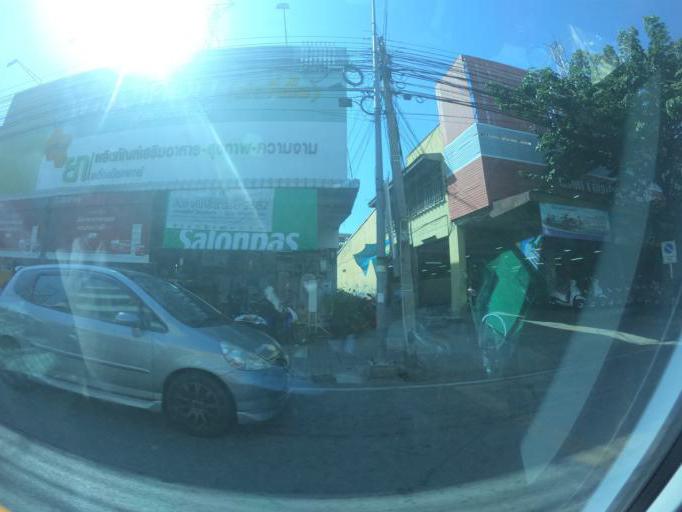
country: TH
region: Khon Kaen
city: Khon Kaen
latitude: 16.3766
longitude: 102.9249
